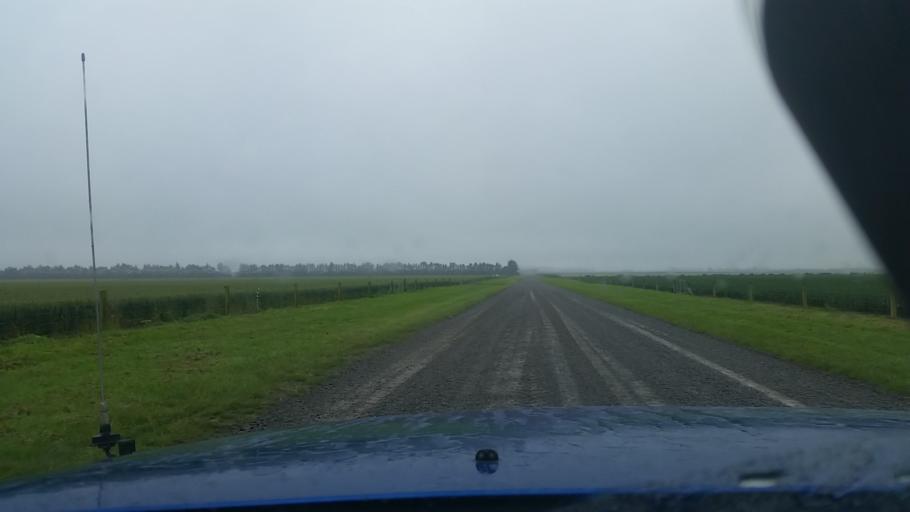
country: NZ
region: Canterbury
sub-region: Ashburton District
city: Rakaia
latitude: -43.7274
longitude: 171.8706
